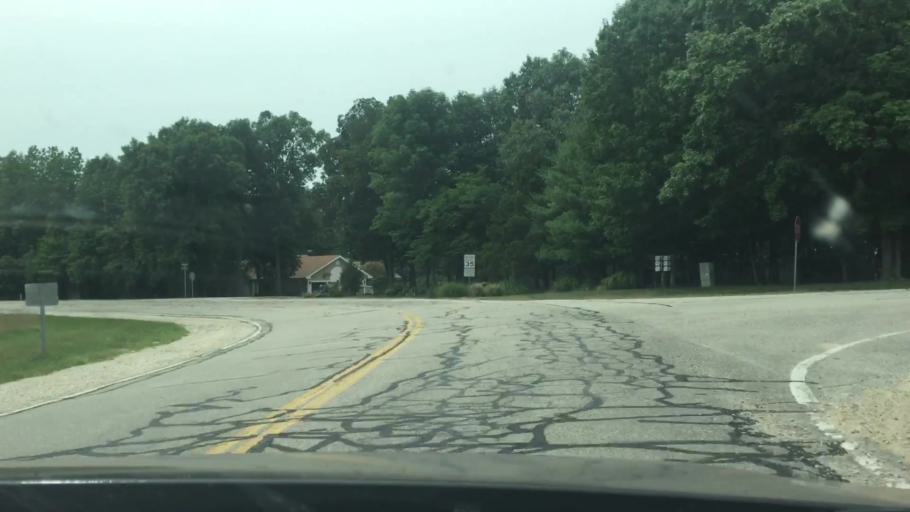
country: US
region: Missouri
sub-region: Camden County
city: Four Seasons
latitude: 38.2002
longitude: -92.7088
